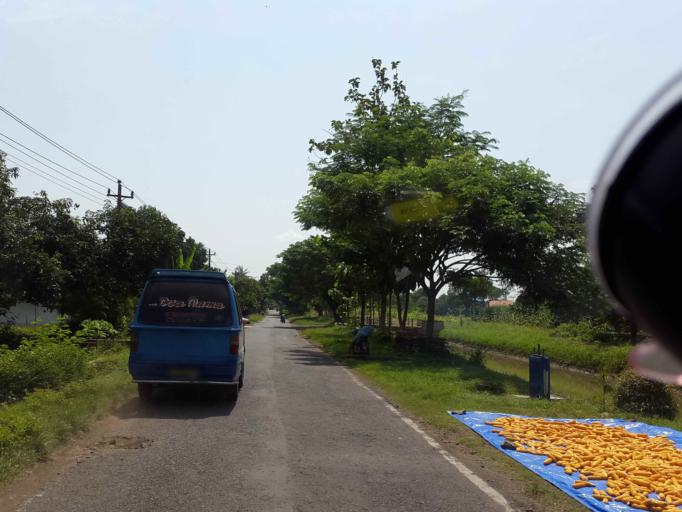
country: ID
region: Central Java
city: Pemalang
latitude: -6.9495
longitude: 109.3683
